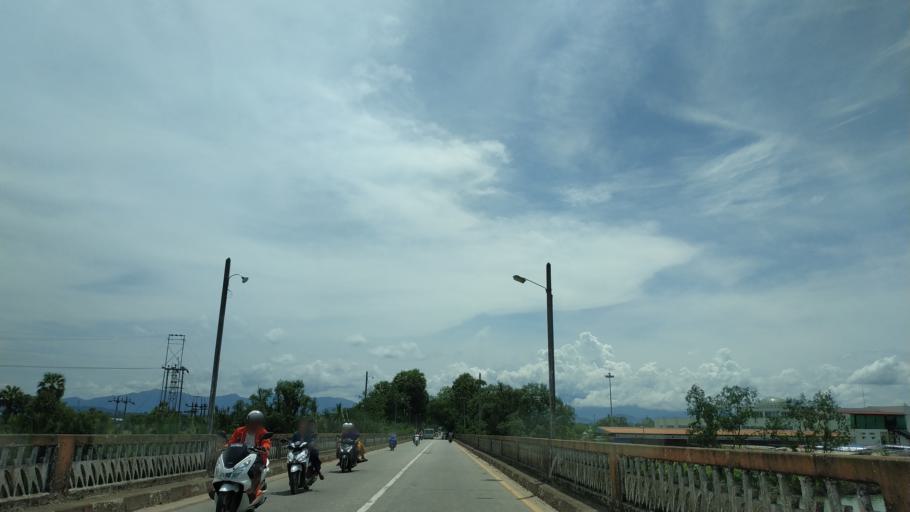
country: MM
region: Tanintharyi
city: Dawei
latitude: 14.0948
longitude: 98.1747
